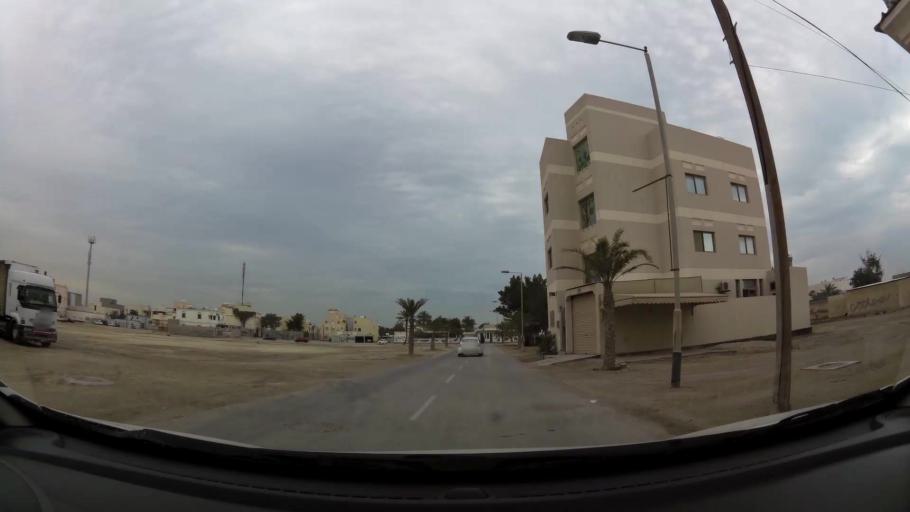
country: BH
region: Manama
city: Manama
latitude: 26.1818
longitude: 50.5850
